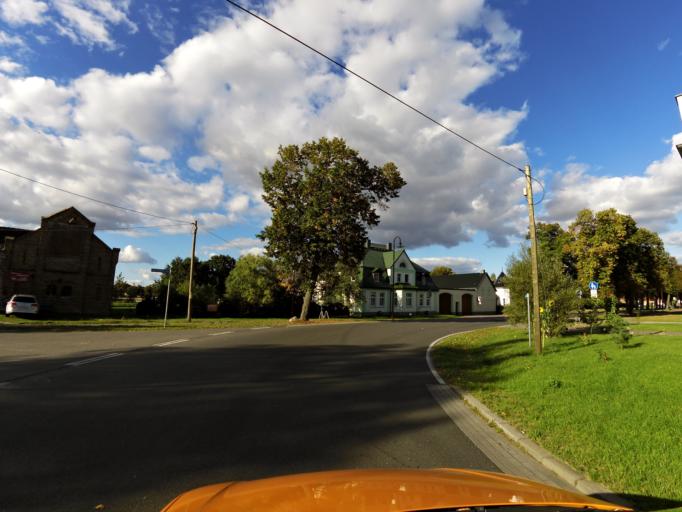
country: DE
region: Brandenburg
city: Trebbin
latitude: 52.1611
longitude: 13.1839
